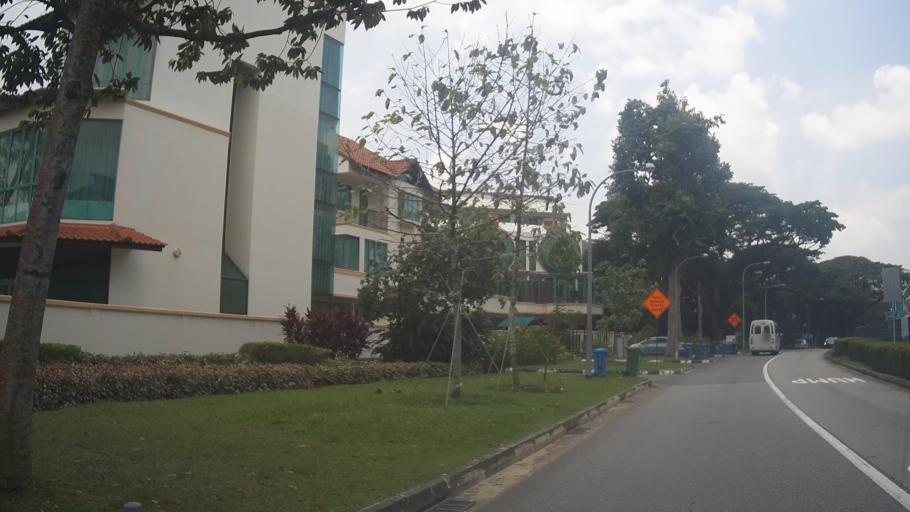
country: SG
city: Singapore
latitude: 1.3391
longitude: 103.7806
